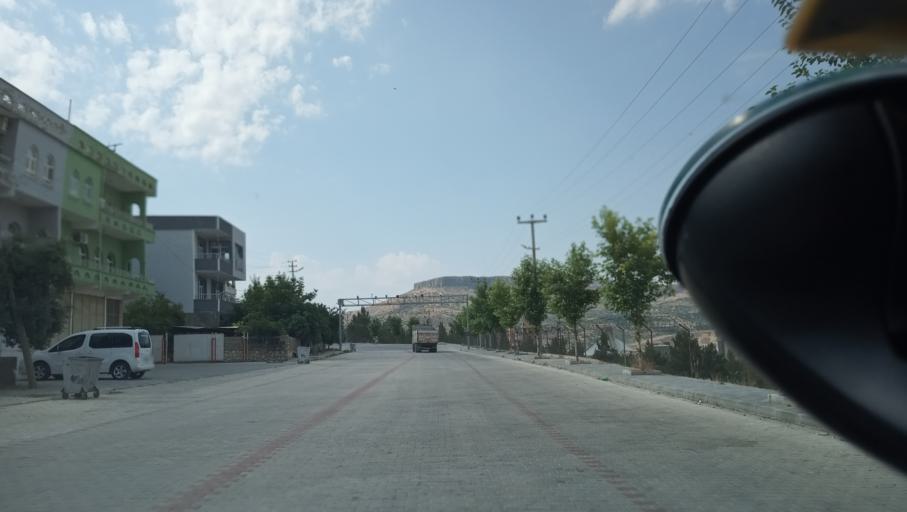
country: TR
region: Mardin
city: Kabala
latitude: 37.3448
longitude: 40.8040
